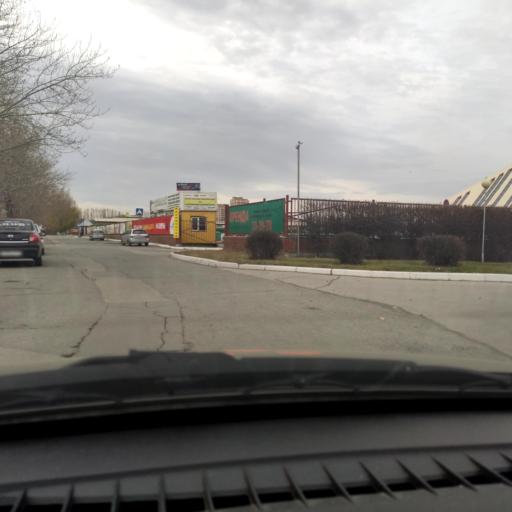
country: RU
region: Samara
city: Tol'yatti
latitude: 53.5422
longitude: 49.2845
